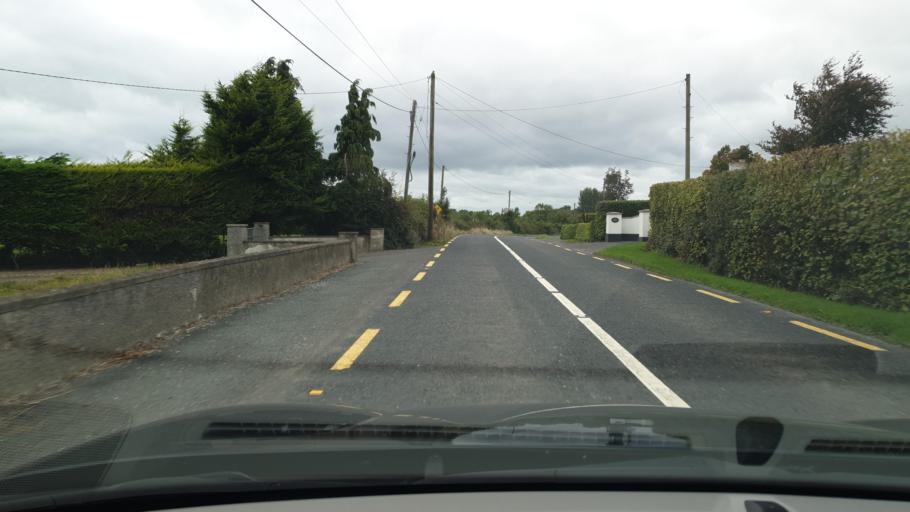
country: IE
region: Leinster
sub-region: Kildare
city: Clane
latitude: 53.2833
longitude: -6.7112
